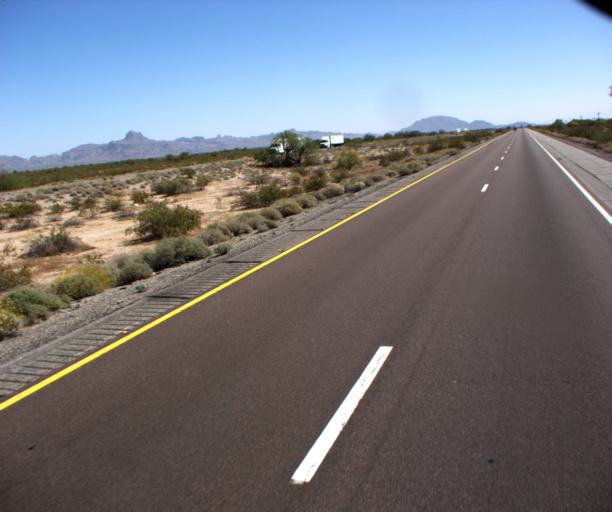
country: US
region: Arizona
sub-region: La Paz County
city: Salome
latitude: 33.5581
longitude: -113.2832
